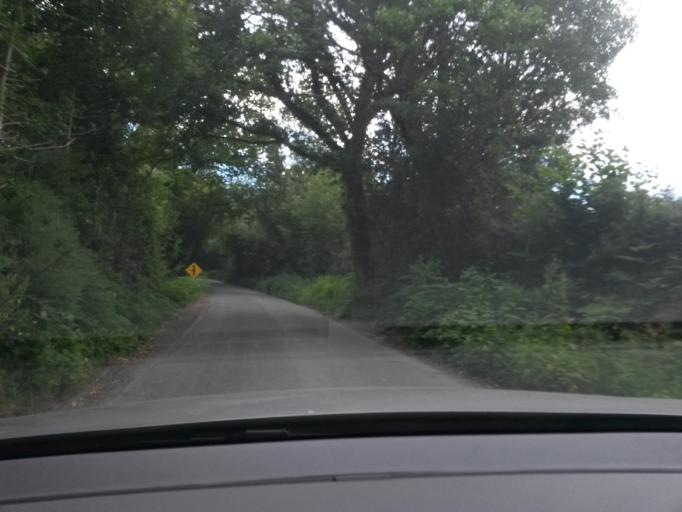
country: IE
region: Leinster
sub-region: Wicklow
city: Enniskerry
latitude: 53.1642
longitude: -6.2142
